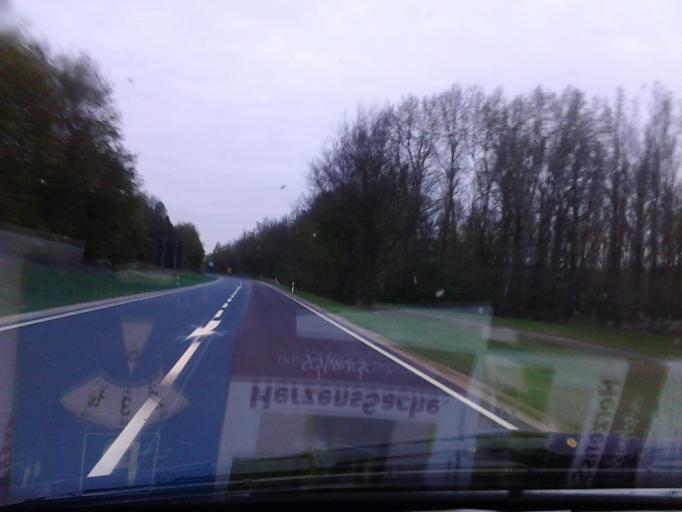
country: DE
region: Bavaria
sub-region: Regierungsbezirk Unterfranken
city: Rentweinsdorf
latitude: 50.1068
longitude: 10.7794
